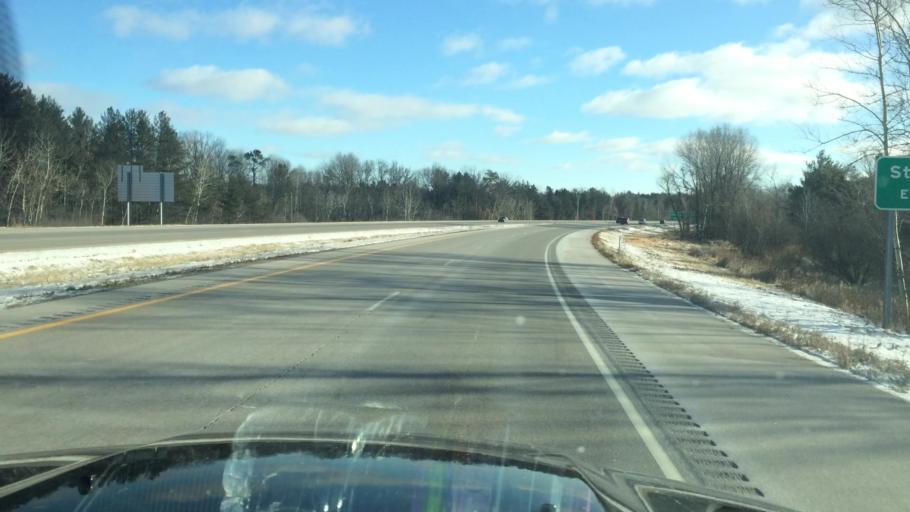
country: US
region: Wisconsin
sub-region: Portage County
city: Stevens Point
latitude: 44.5482
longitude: -89.5576
